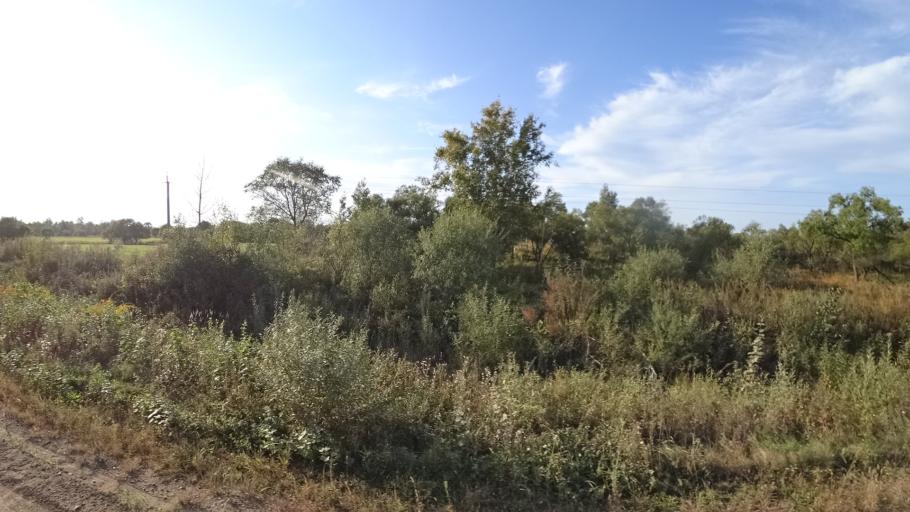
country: RU
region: Amur
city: Arkhara
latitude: 49.3534
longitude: 130.1357
